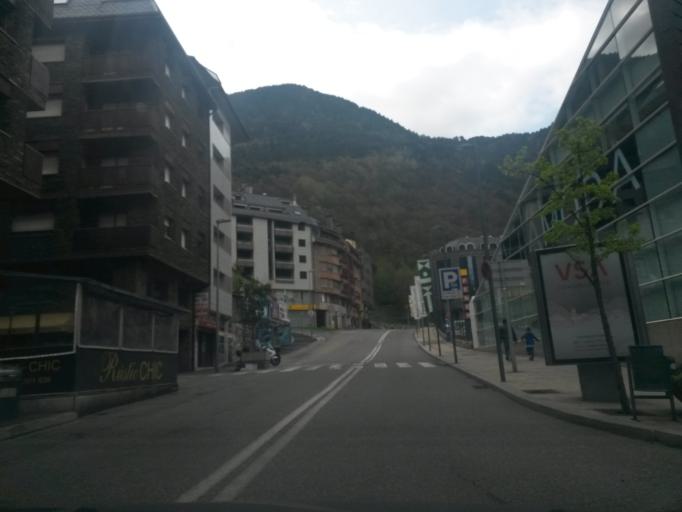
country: AD
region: Escaldes-Engordany
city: les Escaldes
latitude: 42.5080
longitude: 1.5341
